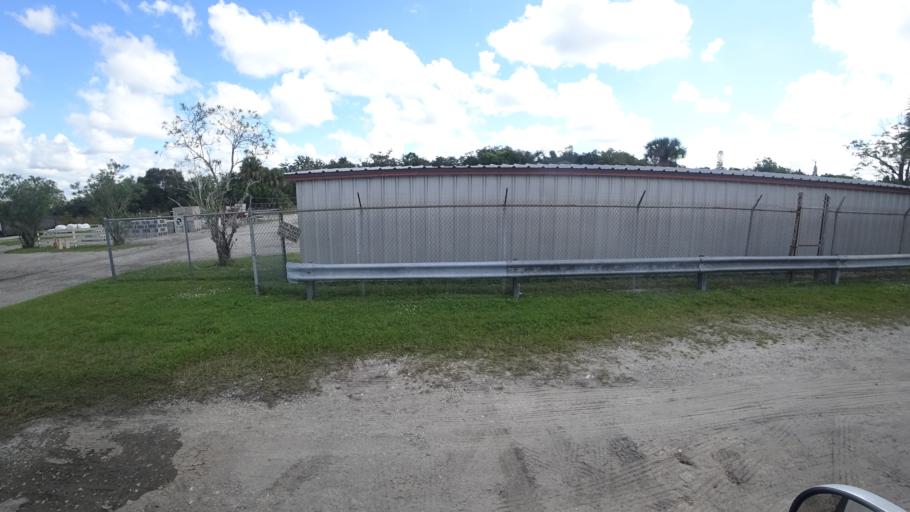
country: US
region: Florida
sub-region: Manatee County
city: West Samoset
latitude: 27.4743
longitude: -82.5502
